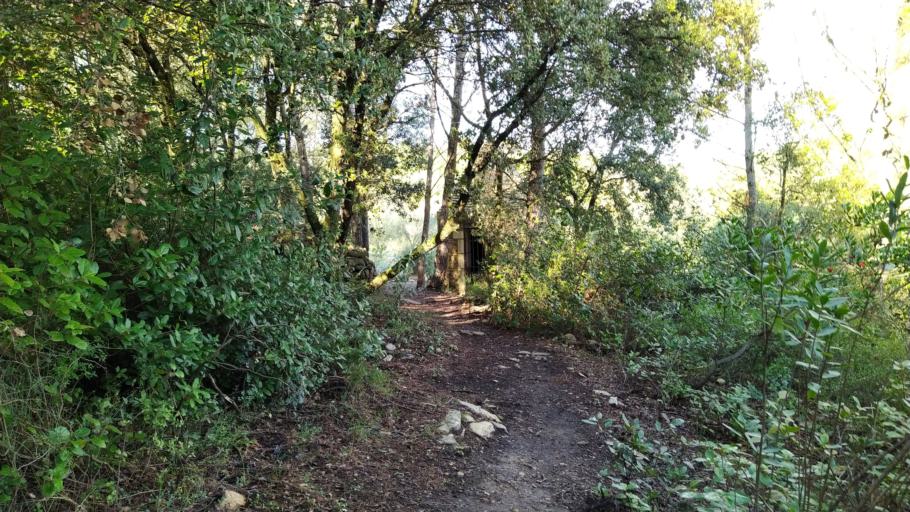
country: FR
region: Languedoc-Roussillon
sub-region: Departement du Gard
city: Poulx
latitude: 43.8731
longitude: 4.4041
